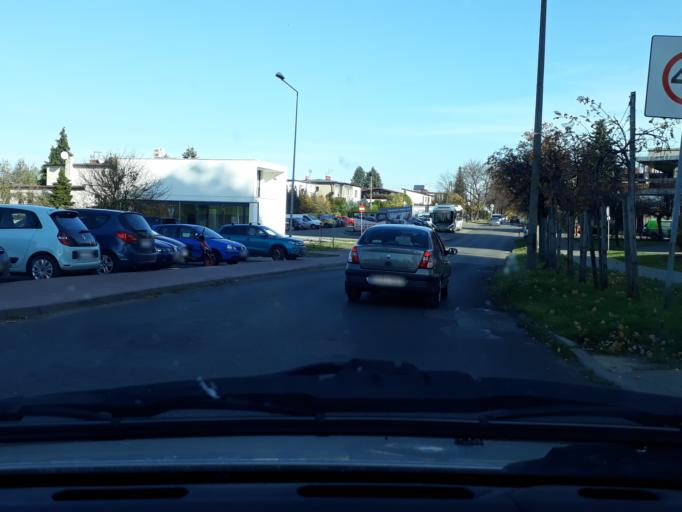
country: PL
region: Silesian Voivodeship
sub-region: Powiat tarnogorski
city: Tarnowskie Gory
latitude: 50.4333
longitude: 18.8658
